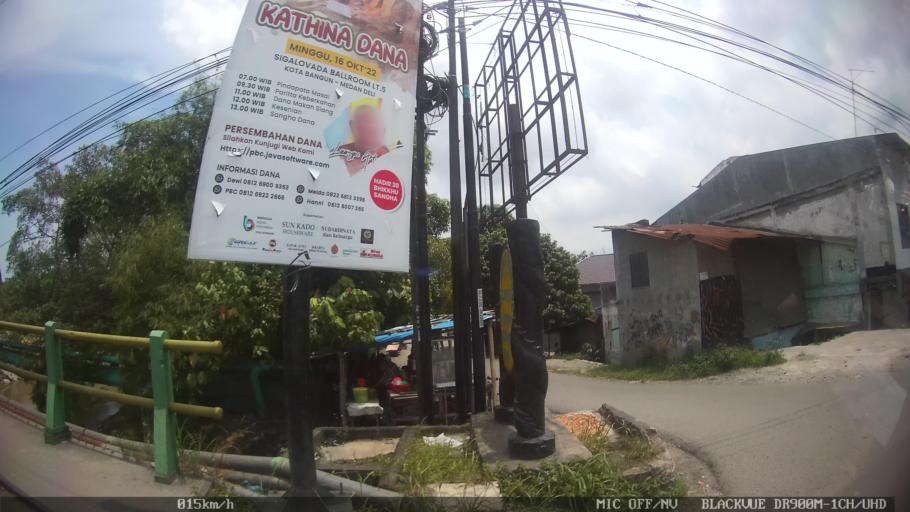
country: ID
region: North Sumatra
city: Labuhan Deli
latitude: 3.6875
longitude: 98.6663
